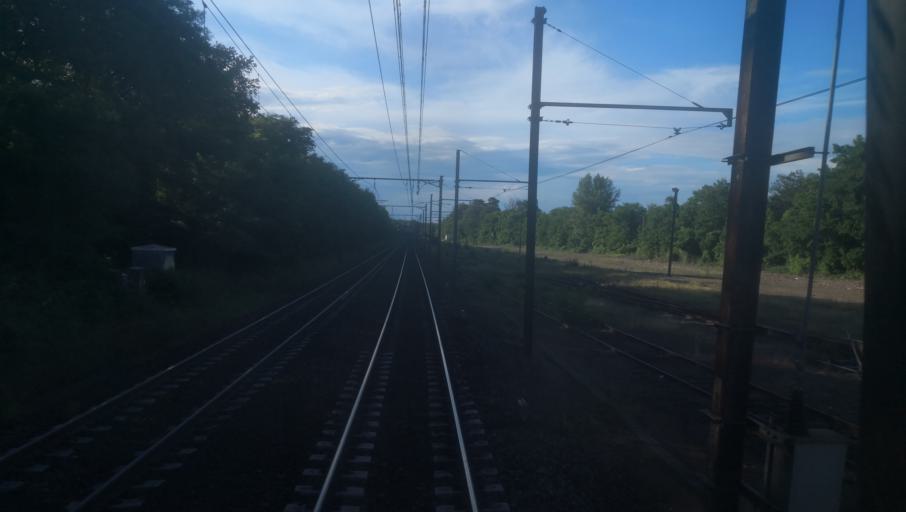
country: FR
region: Centre
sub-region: Departement du Cher
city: Vierzon
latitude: 47.2452
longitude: 2.0456
